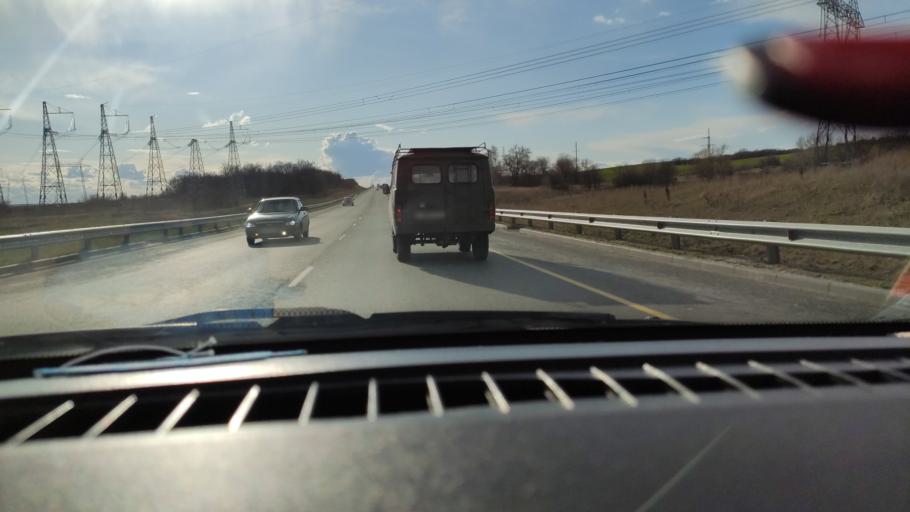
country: RU
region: Saratov
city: Yelshanka
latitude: 51.8237
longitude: 46.3148
